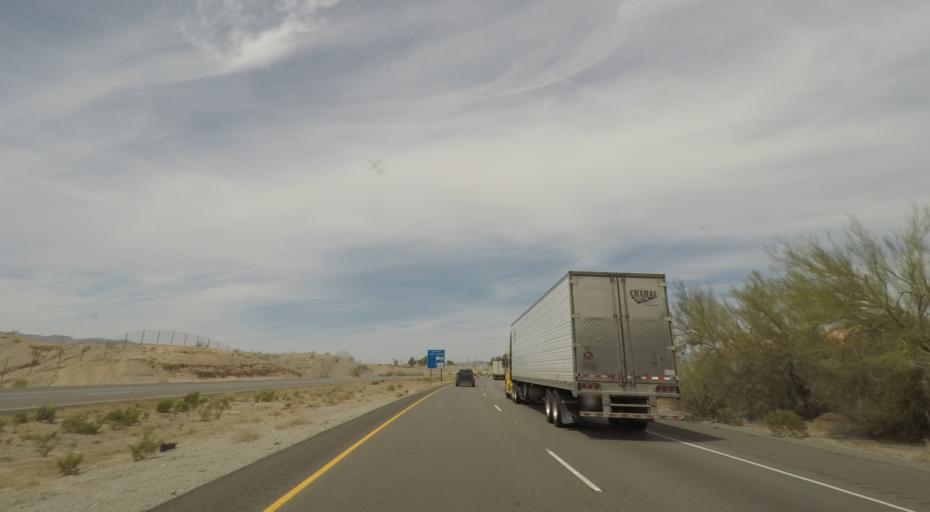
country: US
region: California
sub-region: San Bernardino County
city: Needles
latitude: 34.8337
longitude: -114.6063
